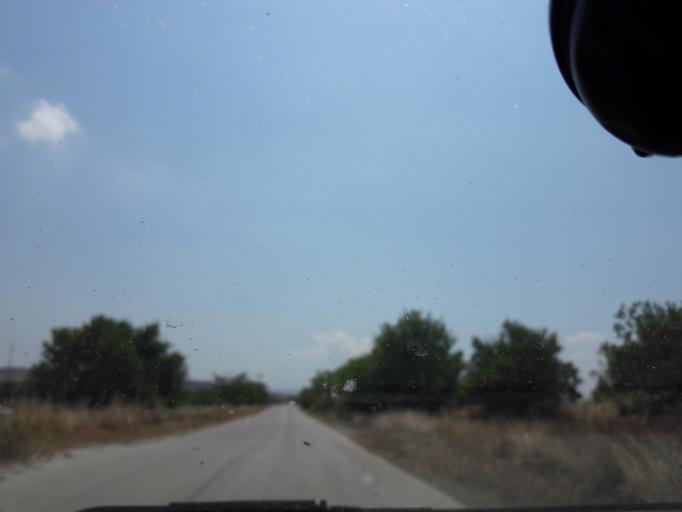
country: GR
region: North Aegean
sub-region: Nomos Lesvou
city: Myrina
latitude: 39.9079
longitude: 25.3095
